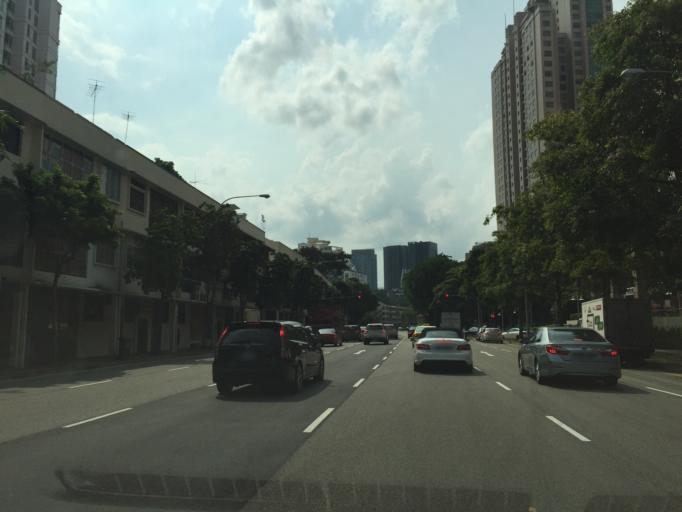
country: SG
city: Singapore
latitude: 1.2933
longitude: 103.8313
